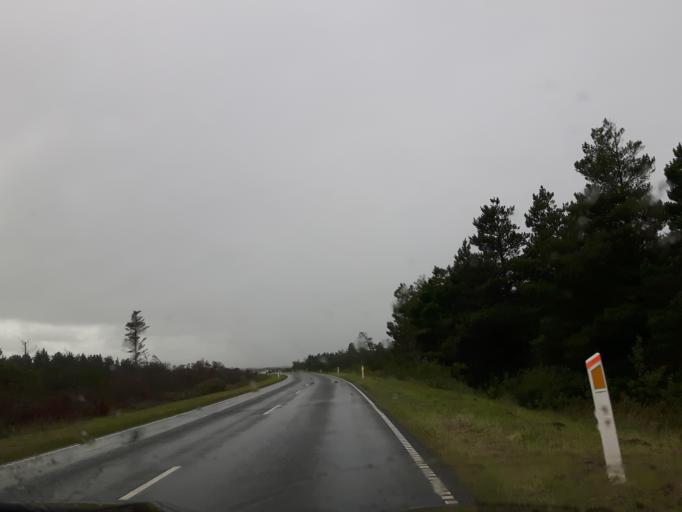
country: DK
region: North Denmark
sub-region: Thisted Kommune
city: Hanstholm
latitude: 57.0220
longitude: 8.4744
